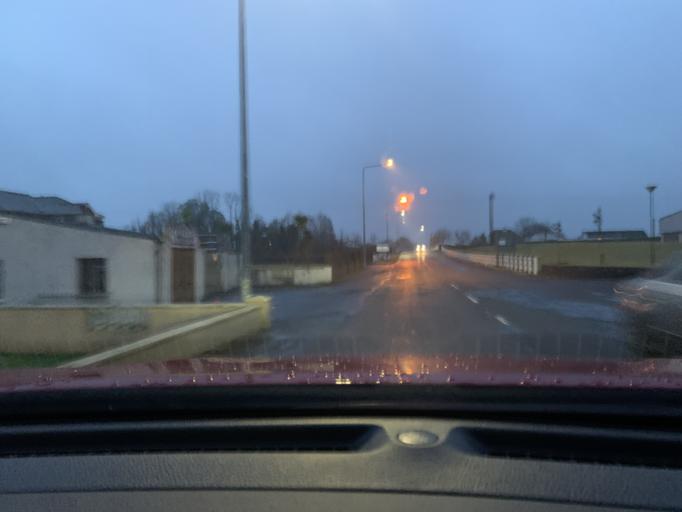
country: IE
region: Connaught
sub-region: Sligo
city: Ballymote
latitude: 53.9974
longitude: -8.5220
